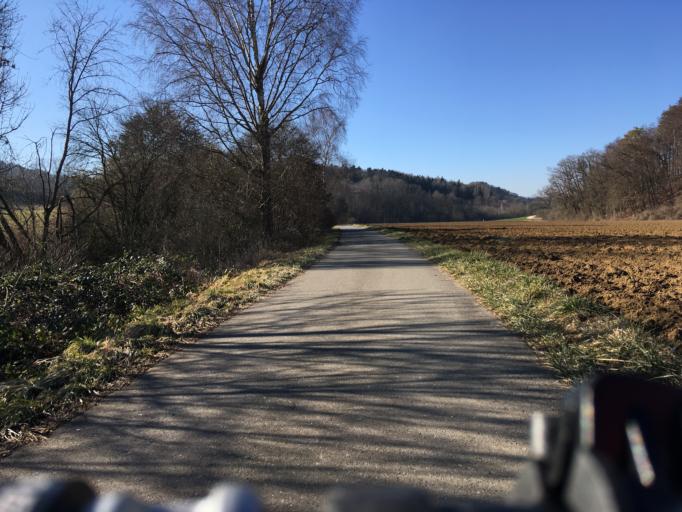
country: DE
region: Baden-Wuerttemberg
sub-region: Freiburg Region
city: Gailingen
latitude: 47.7295
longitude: 8.7421
